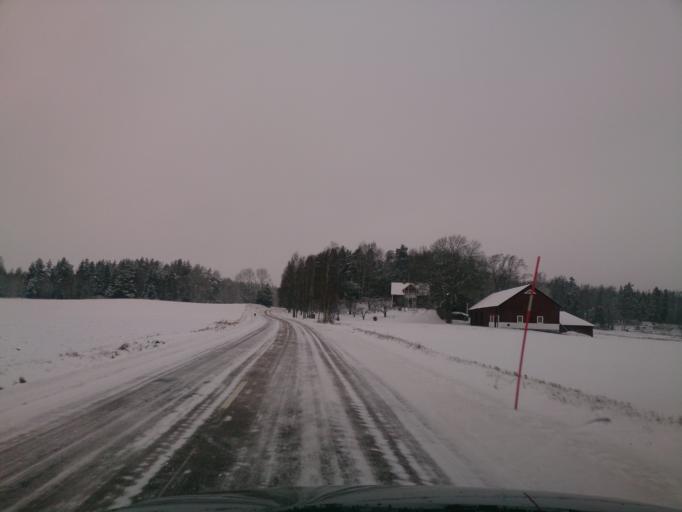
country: SE
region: OEstergoetland
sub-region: Linkopings Kommun
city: Linghem
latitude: 58.4531
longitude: 15.8868
